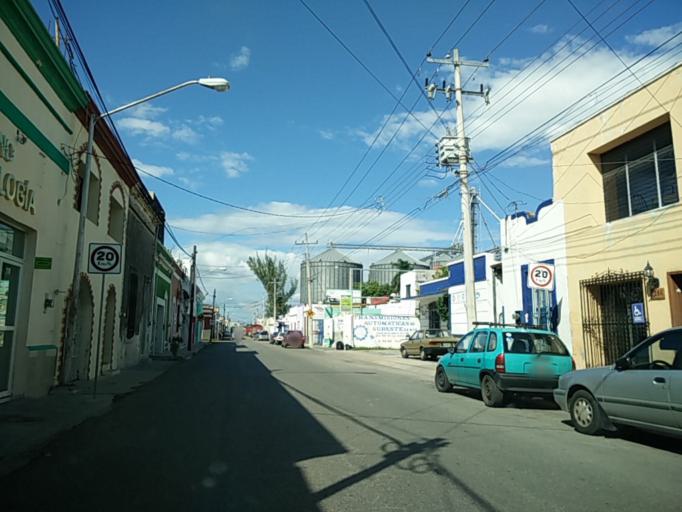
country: MX
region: Yucatan
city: Merida
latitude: 20.9776
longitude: -89.6155
